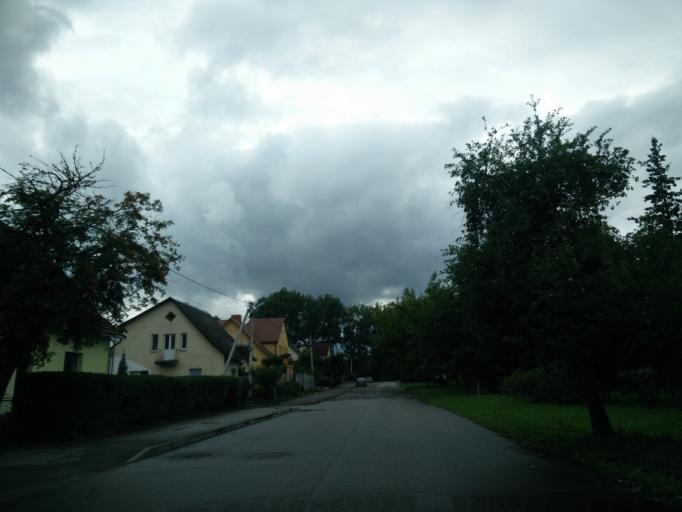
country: LT
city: Grigiskes
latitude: 54.6741
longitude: 25.0892
